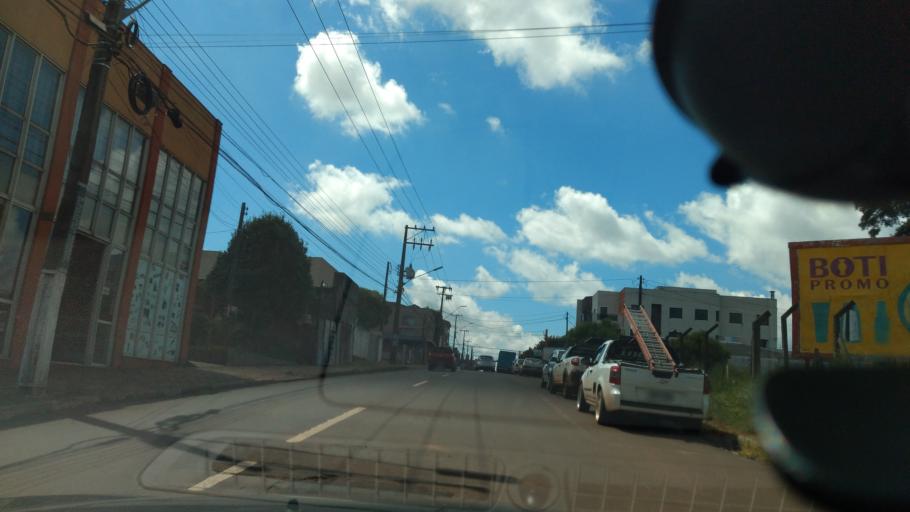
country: BR
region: Parana
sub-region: Guarapuava
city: Guarapuava
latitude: -25.3855
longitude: -51.4798
